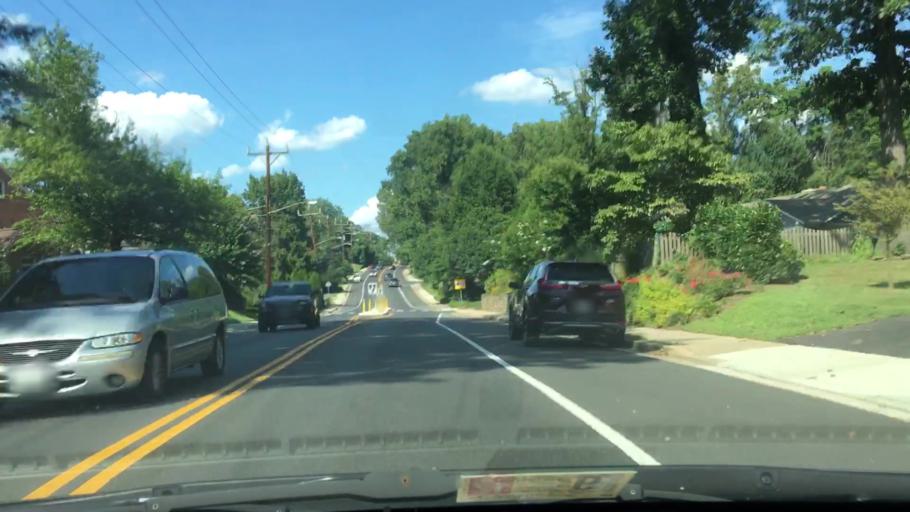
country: US
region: Maryland
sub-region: Montgomery County
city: South Kensington
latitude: 39.0169
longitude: -77.0877
